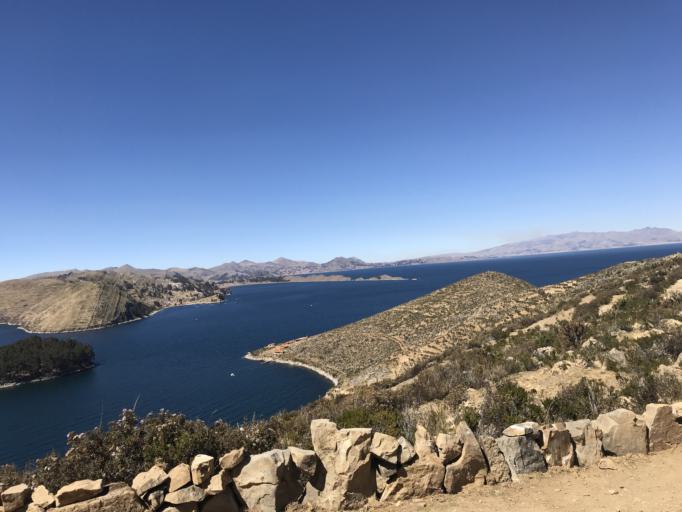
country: BO
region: La Paz
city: Yumani
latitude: -16.0446
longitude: -69.1460
